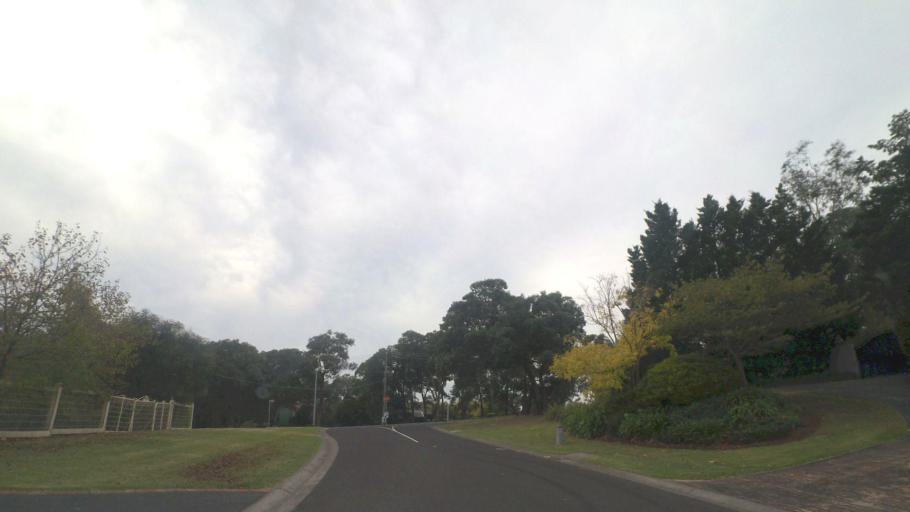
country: AU
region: Victoria
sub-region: Nillumbik
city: North Warrandyte
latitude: -37.7497
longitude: 145.1908
